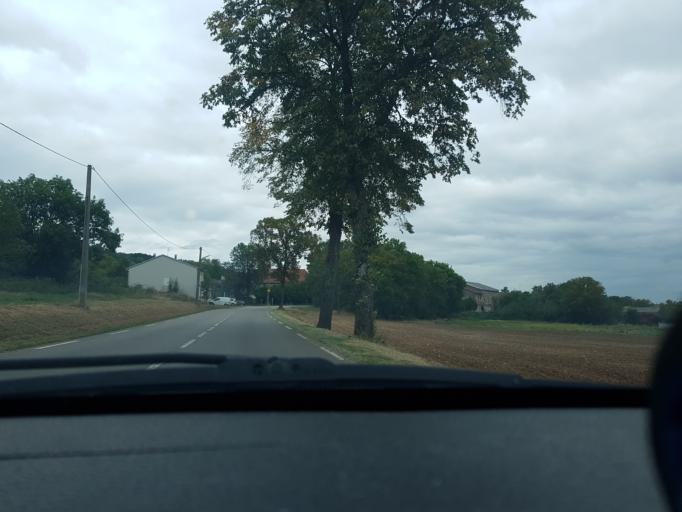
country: FR
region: Lorraine
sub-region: Departement de la Moselle
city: Chateau-Salins
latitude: 48.8497
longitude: 6.5113
